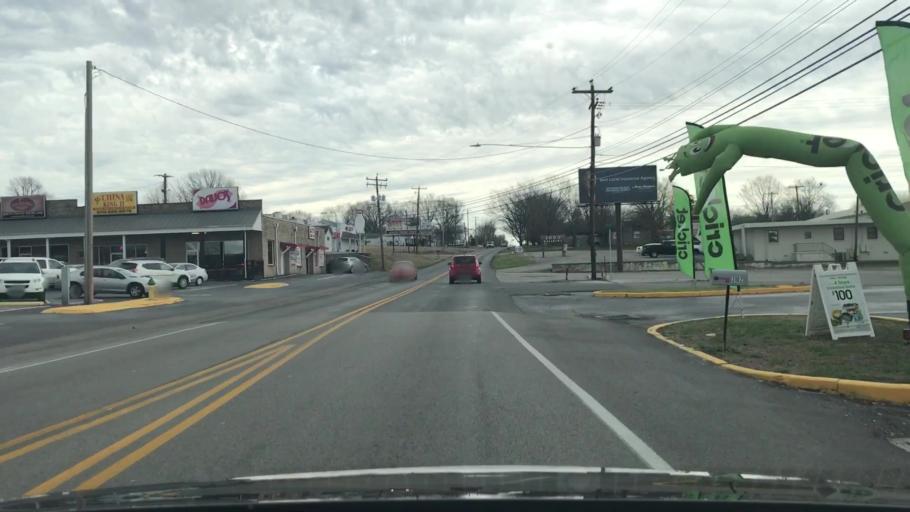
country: US
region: Kentucky
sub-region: Christian County
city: Hopkinsville
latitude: 36.8605
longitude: -87.5142
